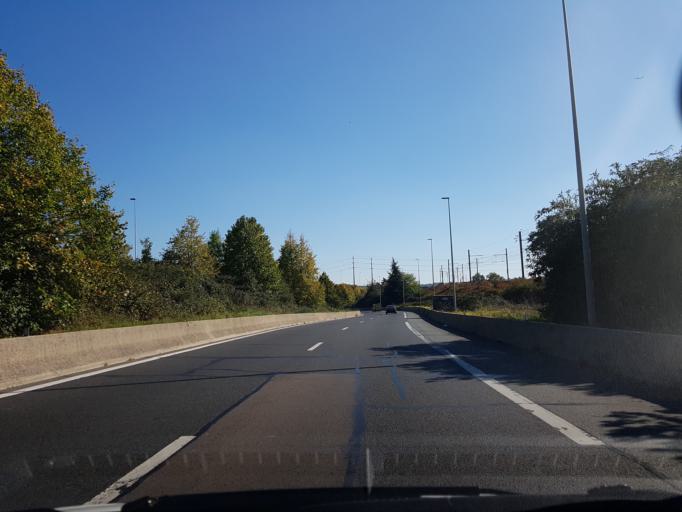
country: FR
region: Ile-de-France
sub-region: Departement du Val-de-Marne
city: Bonneuil-sur-Marne
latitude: 48.7629
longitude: 2.4654
